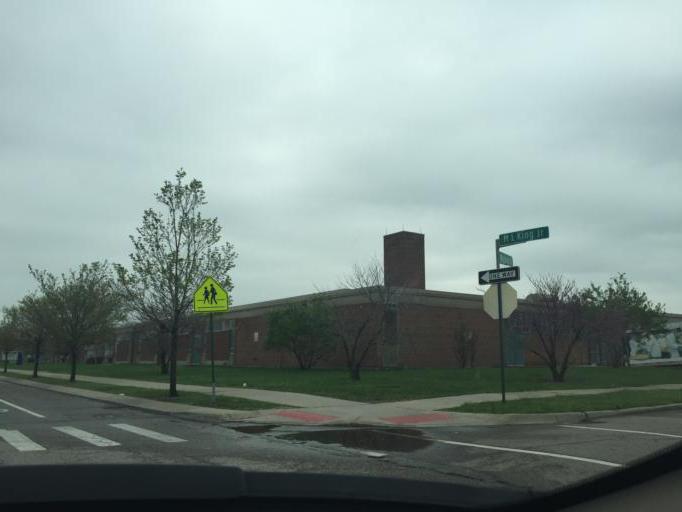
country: US
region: Michigan
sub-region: Wayne County
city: Detroit
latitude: 42.3396
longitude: -83.0797
